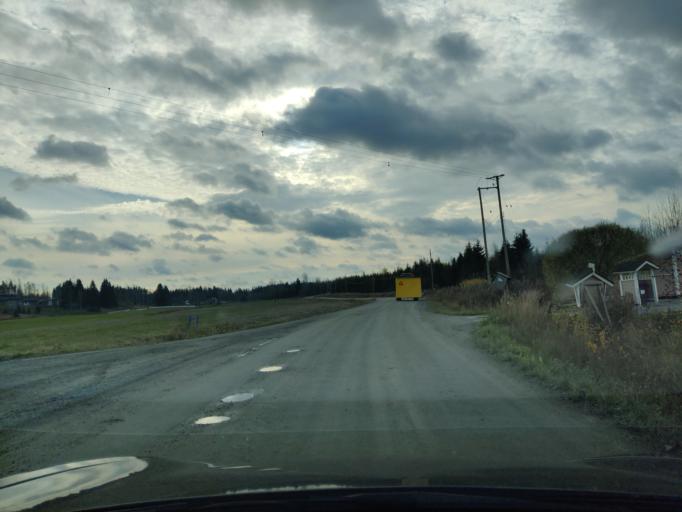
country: FI
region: Northern Savo
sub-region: Kuopio
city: Siilinjaervi
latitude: 63.1070
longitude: 27.5569
